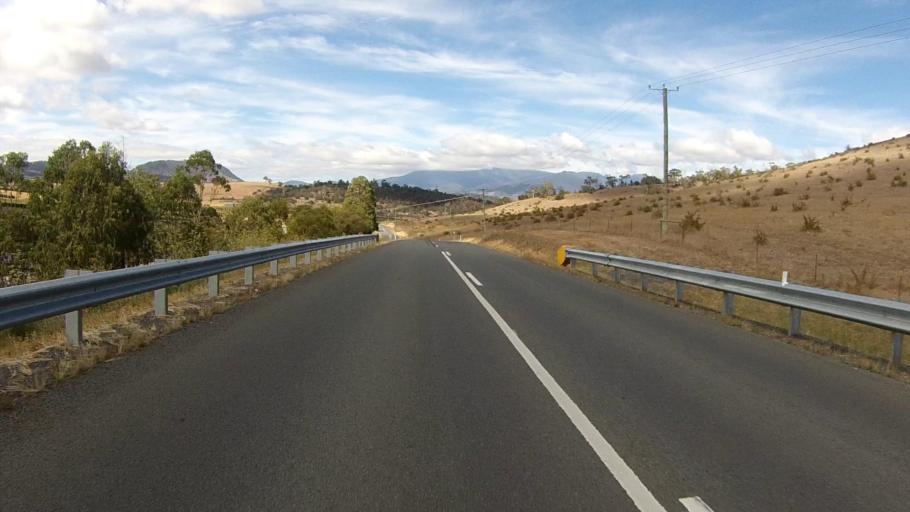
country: AU
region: Tasmania
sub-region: Brighton
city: Old Beach
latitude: -42.7356
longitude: 147.2888
